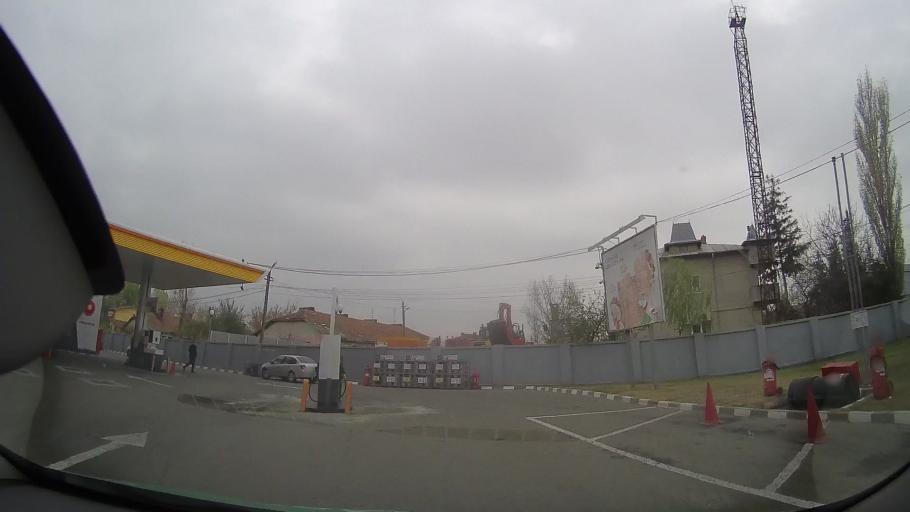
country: RO
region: Ialomita
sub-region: Municipiul Urziceni
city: Urziceni
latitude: 44.7146
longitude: 26.6516
